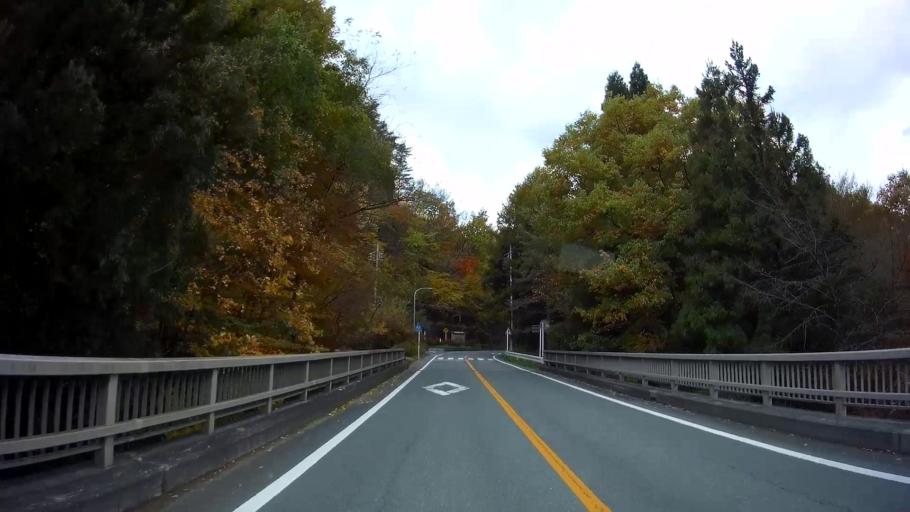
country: JP
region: Gunma
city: Nakanojomachi
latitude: 36.5688
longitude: 138.6335
